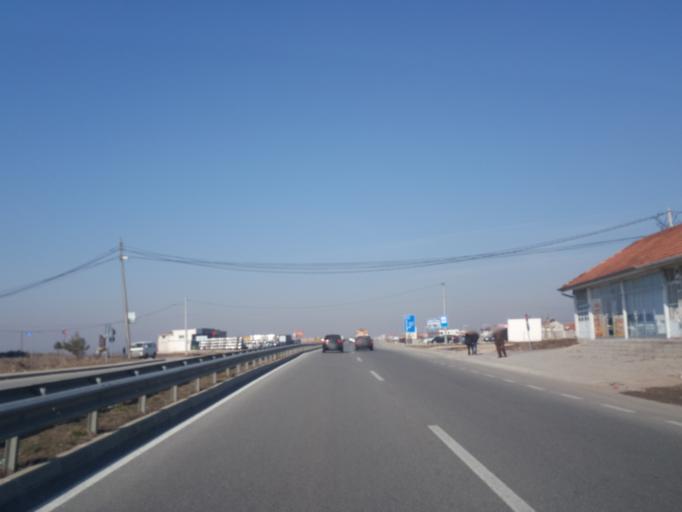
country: XK
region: Pristina
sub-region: Komuna e Obiliqit
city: Obiliq
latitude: 42.7586
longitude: 21.0327
